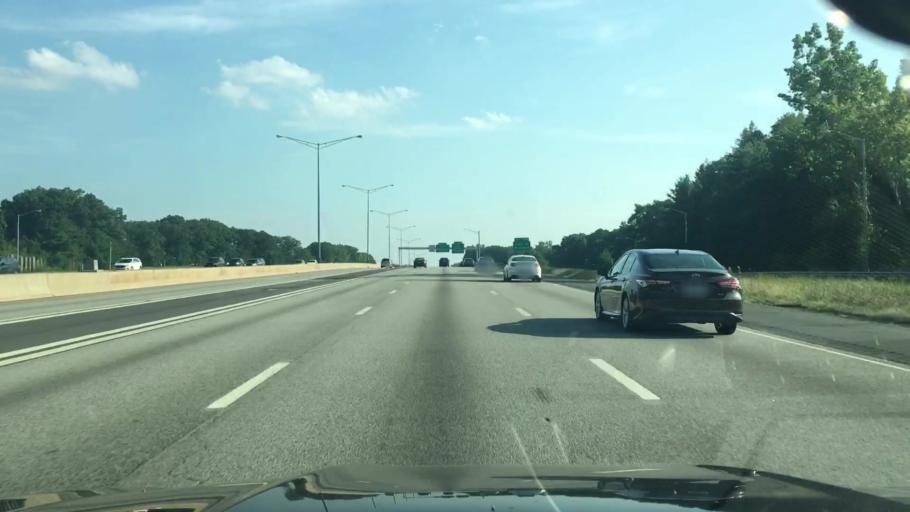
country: US
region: Connecticut
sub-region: Hartford County
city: Windsor
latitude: 41.8409
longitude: -72.6657
